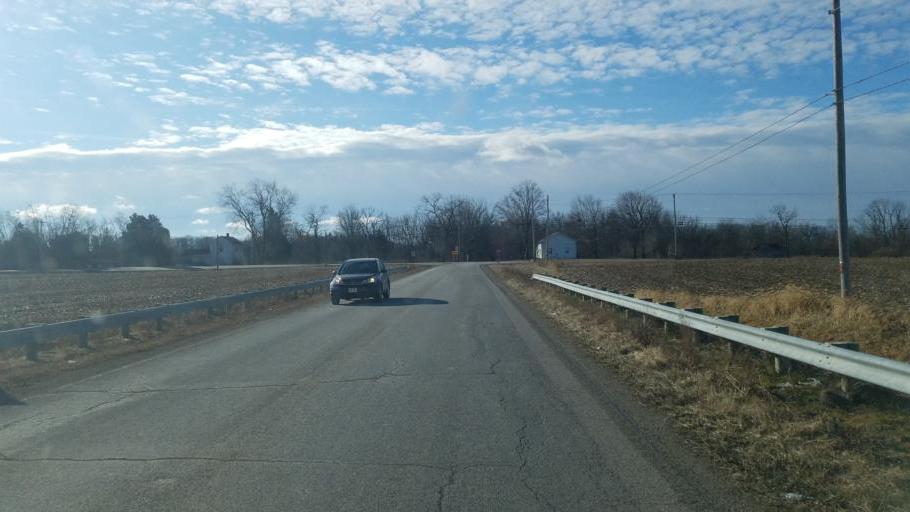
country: US
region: Ohio
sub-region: Morrow County
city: Cardington
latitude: 40.5179
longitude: -82.8642
